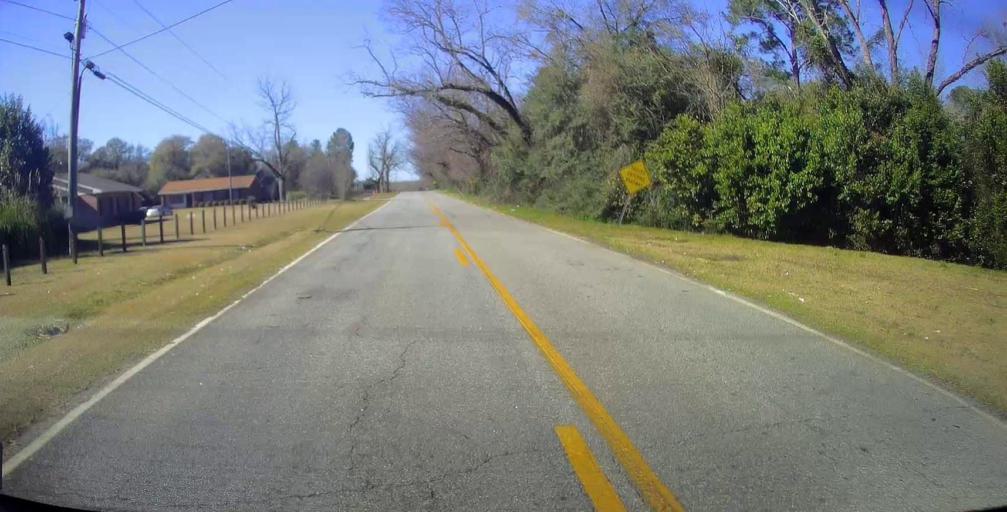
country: US
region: Georgia
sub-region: Macon County
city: Montezuma
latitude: 32.2811
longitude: -84.0288
